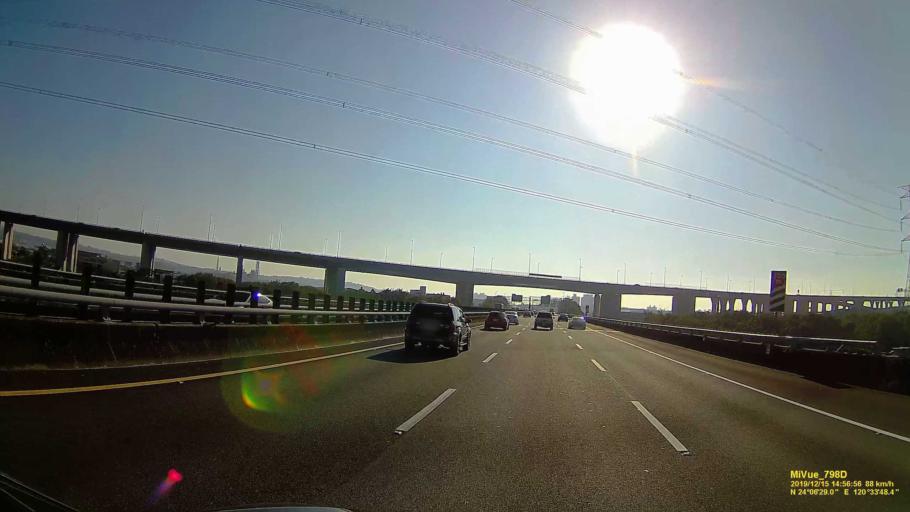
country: TW
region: Taiwan
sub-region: Changhua
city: Chang-hua
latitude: 24.1111
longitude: 120.5664
